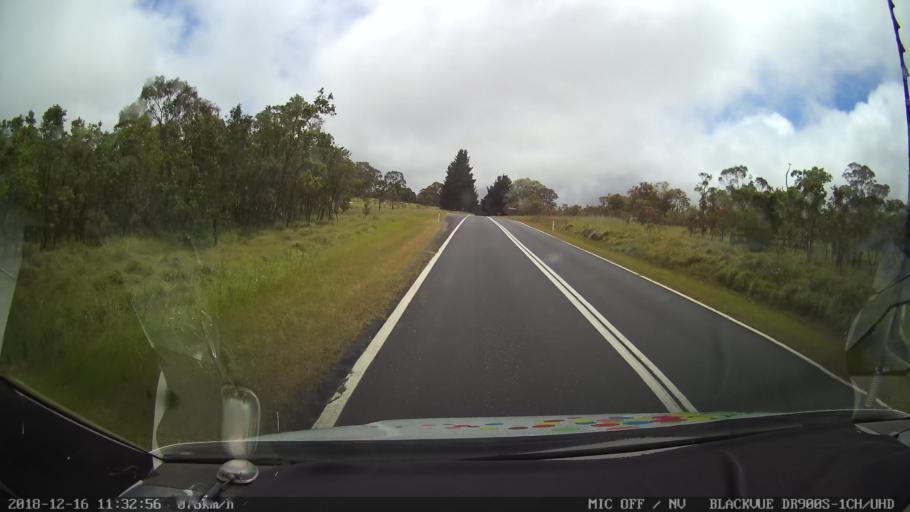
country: AU
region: New South Wales
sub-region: Tenterfield Municipality
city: Carrolls Creek
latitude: -29.0115
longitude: 152.1406
